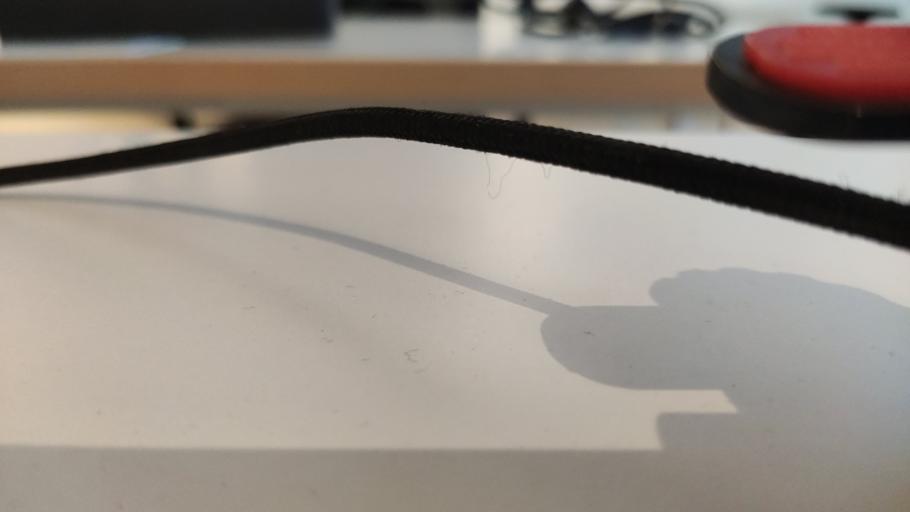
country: RU
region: Moskovskaya
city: Novopetrovskoye
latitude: 55.8726
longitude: 36.4019
